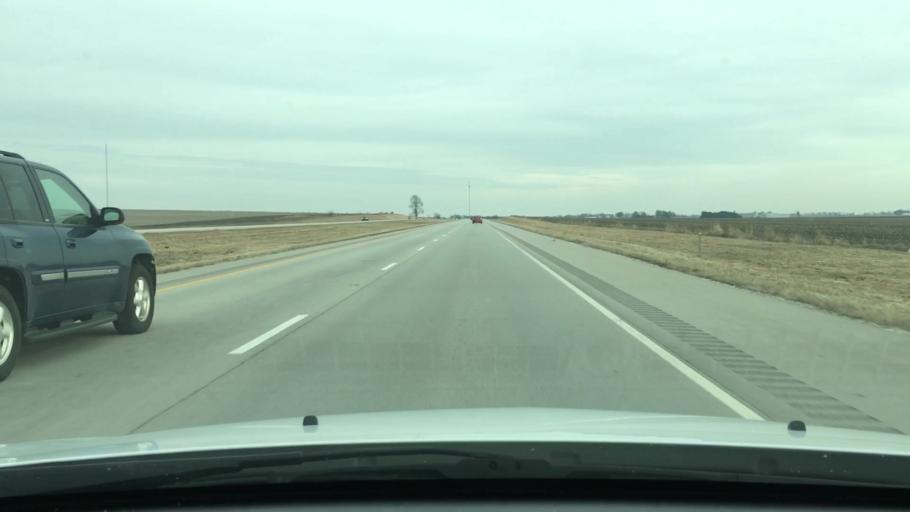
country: US
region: Illinois
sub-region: Morgan County
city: Jacksonville
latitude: 39.7375
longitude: -90.1017
